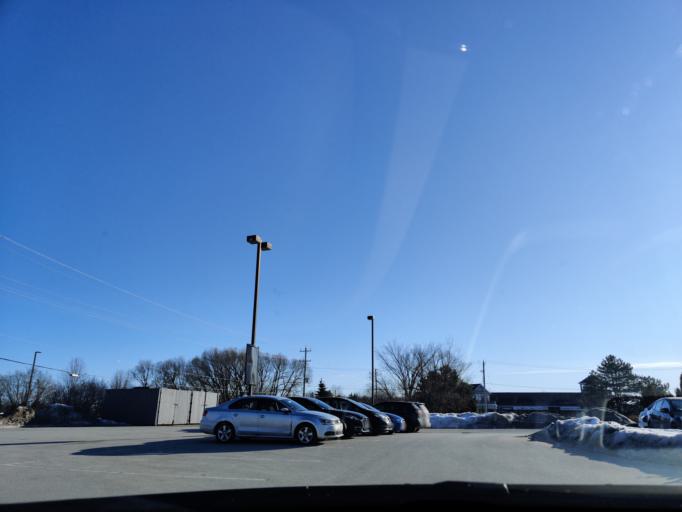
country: CA
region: Ontario
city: Collingwood
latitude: 44.5028
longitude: -80.2265
